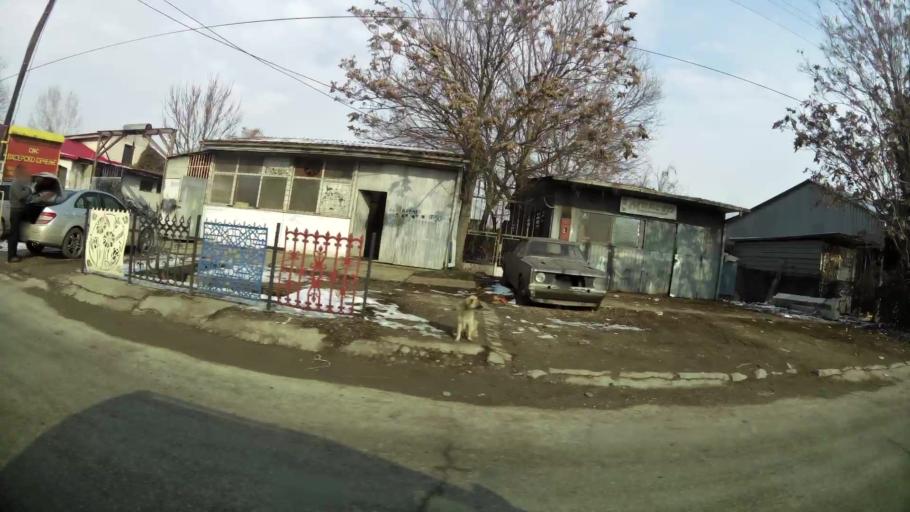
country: MK
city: Krushopek
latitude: 42.0132
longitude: 21.3770
